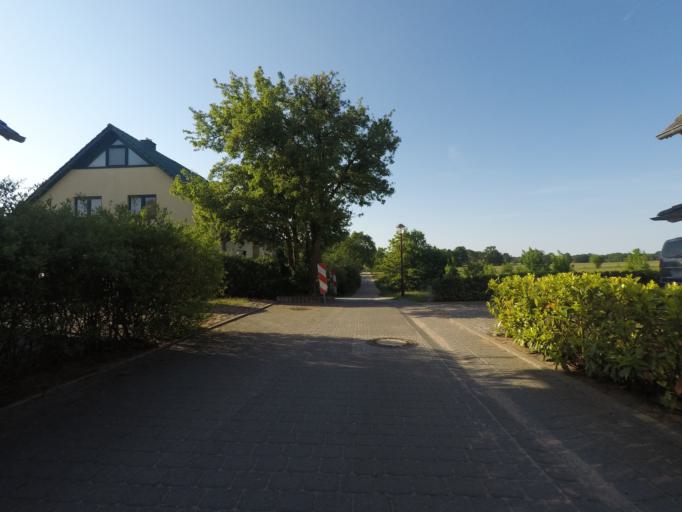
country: DE
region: Brandenburg
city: Joachimsthal
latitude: 52.8941
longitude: 13.7057
